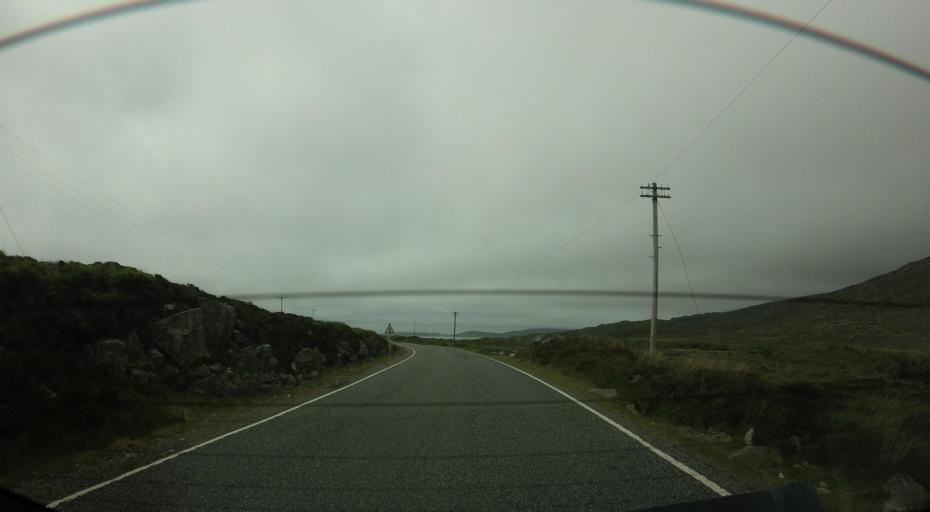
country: GB
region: Scotland
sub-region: Eilean Siar
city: Harris
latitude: 57.8675
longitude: -6.8916
